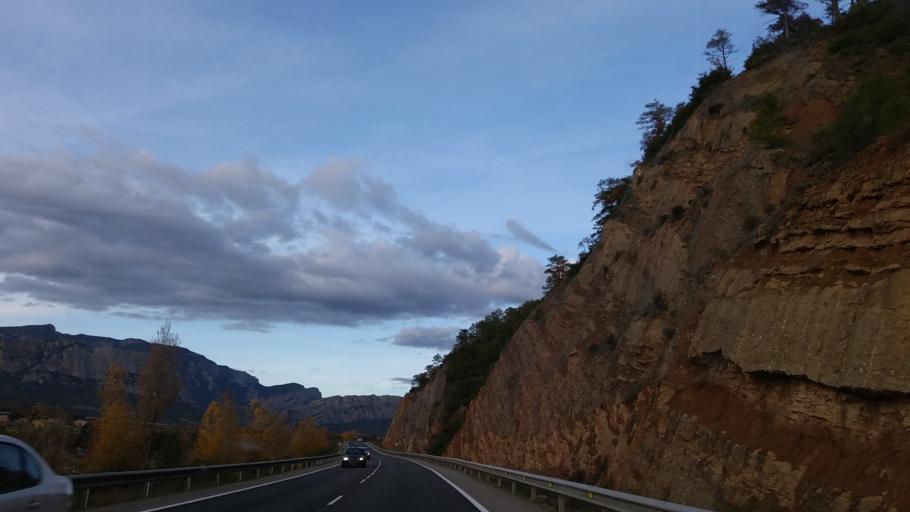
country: ES
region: Catalonia
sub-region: Provincia de Lleida
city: Oliana
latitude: 42.0354
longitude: 1.2953
